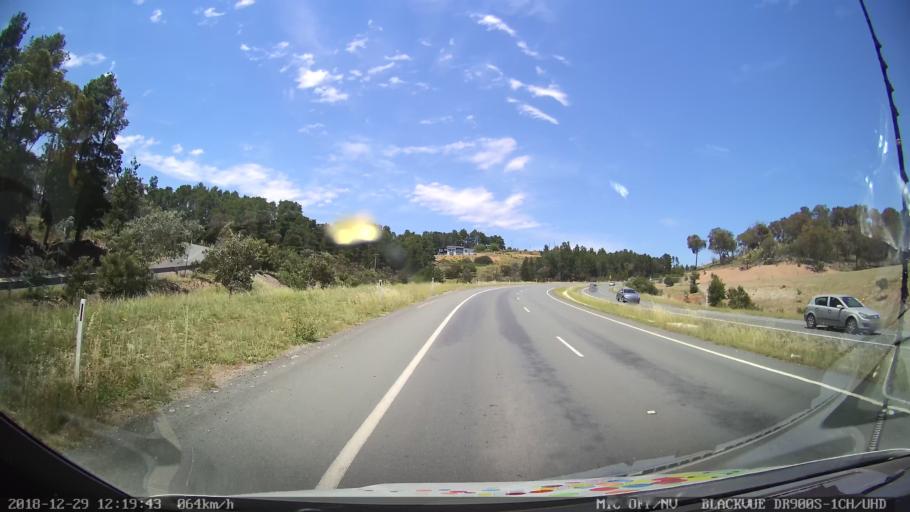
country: AU
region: New South Wales
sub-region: Queanbeyan
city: Queanbeyan
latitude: -35.3965
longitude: 149.2335
